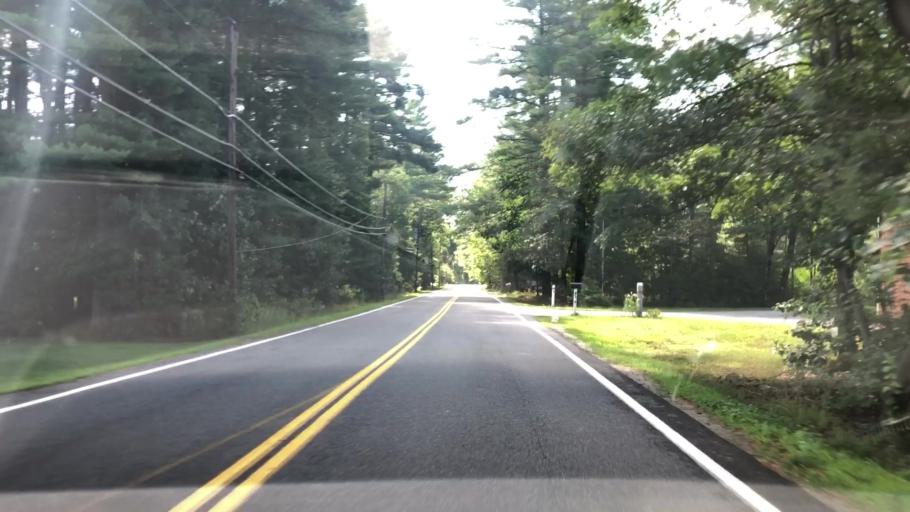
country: US
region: New Hampshire
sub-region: Hillsborough County
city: Milford
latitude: 42.8373
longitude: -71.5979
